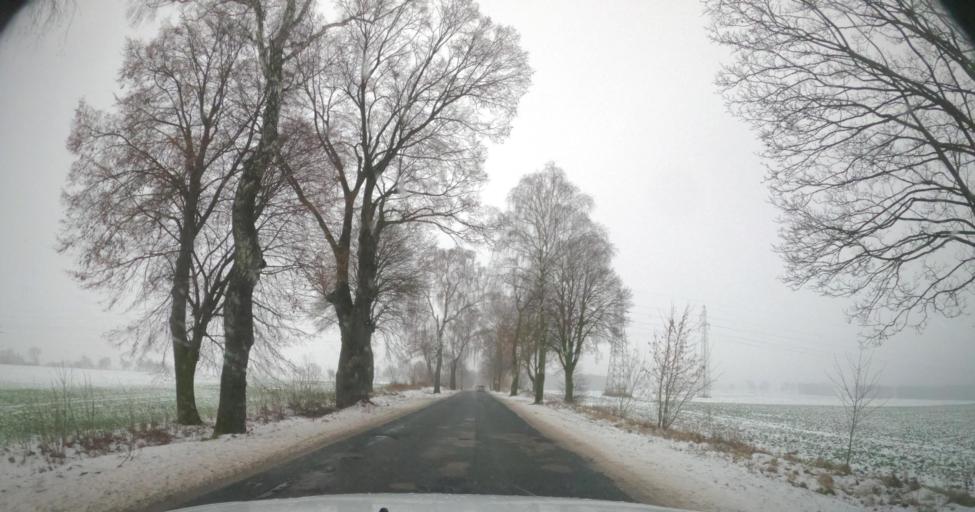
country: PL
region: West Pomeranian Voivodeship
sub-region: Powiat gryficki
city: Gryfice
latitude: 53.9098
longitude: 15.2371
